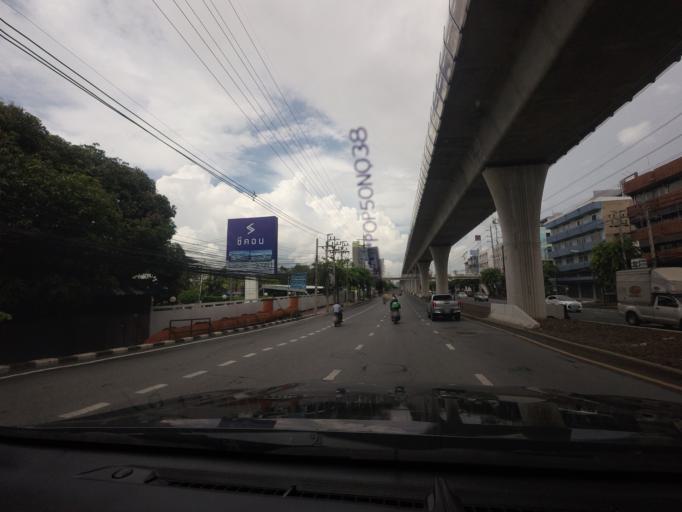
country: TH
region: Bangkok
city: Phasi Charoen
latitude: 13.7114
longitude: 100.4176
